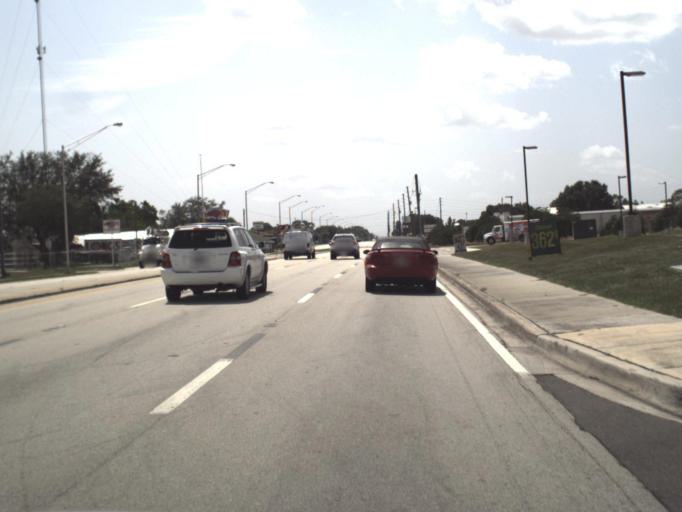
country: US
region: Florida
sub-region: Highlands County
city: Avon Park
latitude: 27.6064
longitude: -81.5146
